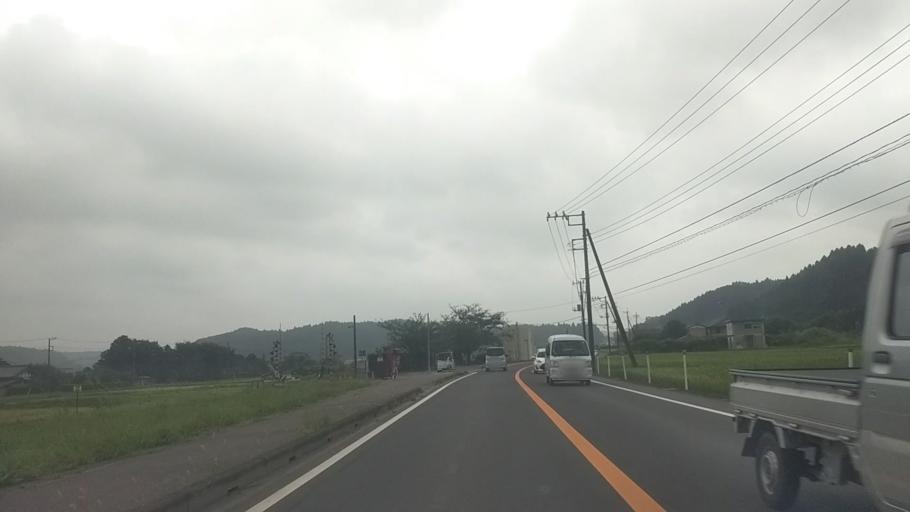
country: JP
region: Chiba
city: Ohara
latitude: 35.2771
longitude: 140.3271
